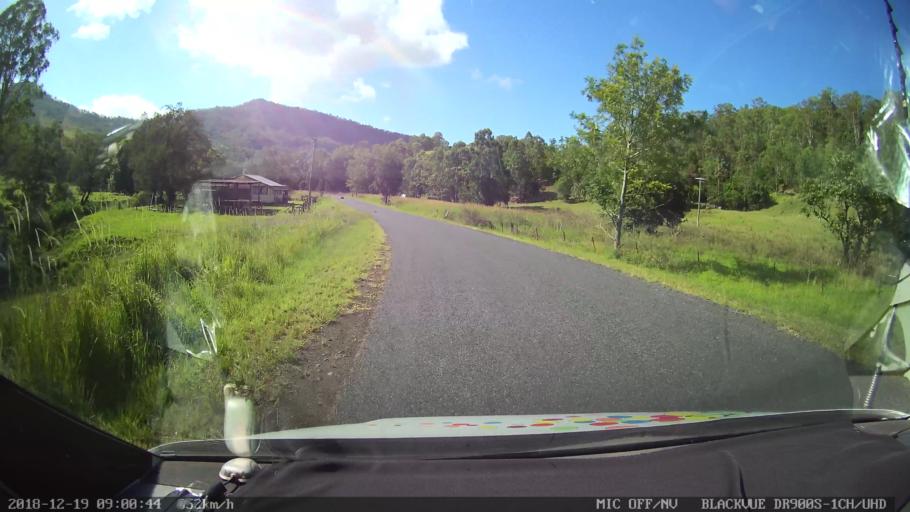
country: AU
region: New South Wales
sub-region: Kyogle
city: Kyogle
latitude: -28.4341
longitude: 152.9566
